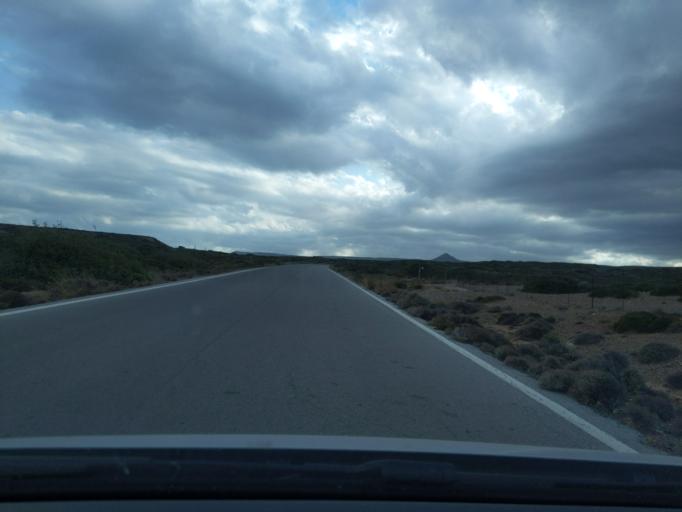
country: GR
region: Crete
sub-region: Nomos Lasithiou
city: Palekastro
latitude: 35.2465
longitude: 26.2497
